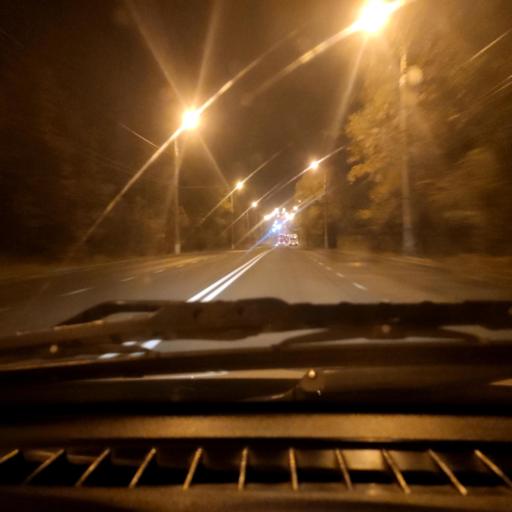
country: RU
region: Samara
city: Zhigulevsk
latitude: 53.5024
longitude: 49.4634
